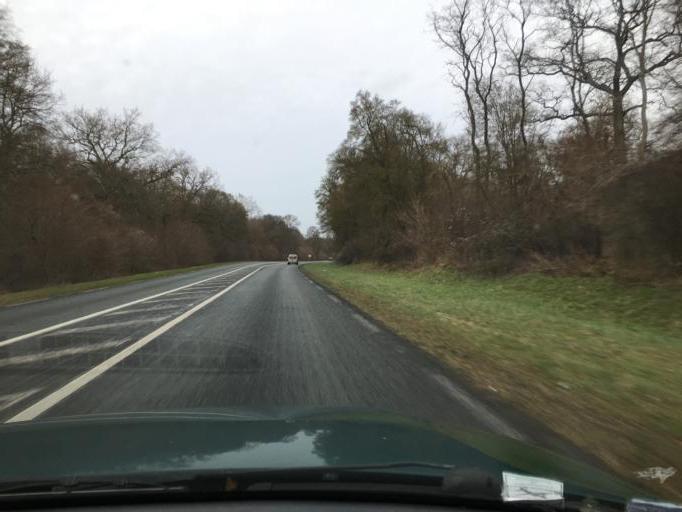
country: FR
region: Picardie
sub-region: Departement de l'Oise
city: Thiers-sur-Theve
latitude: 49.1591
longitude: 2.5522
